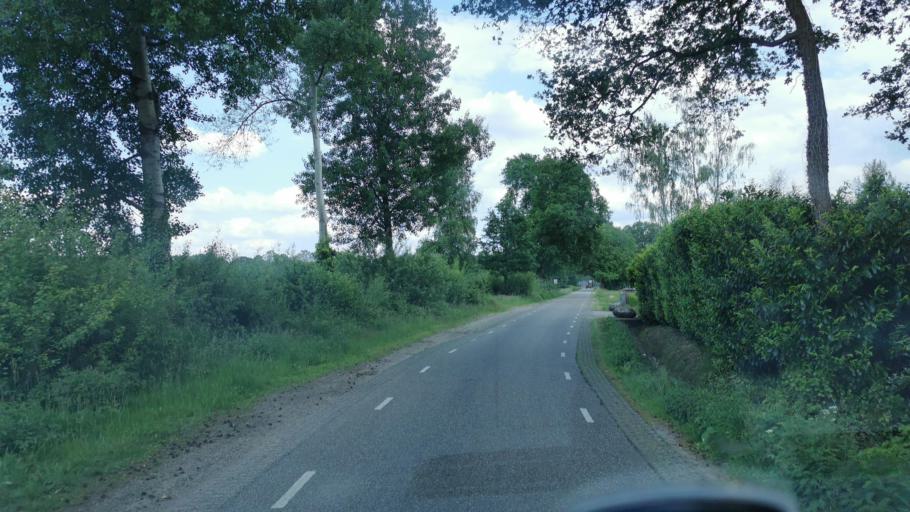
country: NL
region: Overijssel
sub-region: Gemeente Hengelo
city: Hengelo
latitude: 52.3291
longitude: 6.8228
